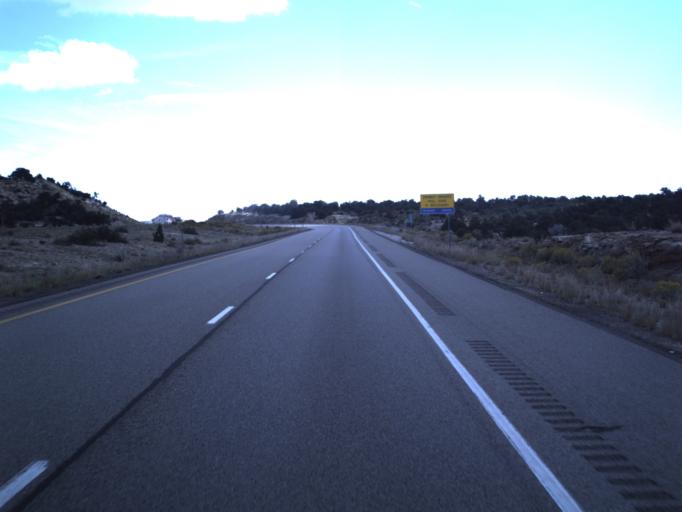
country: US
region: Utah
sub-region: Emery County
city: Ferron
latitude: 38.8623
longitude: -110.8433
